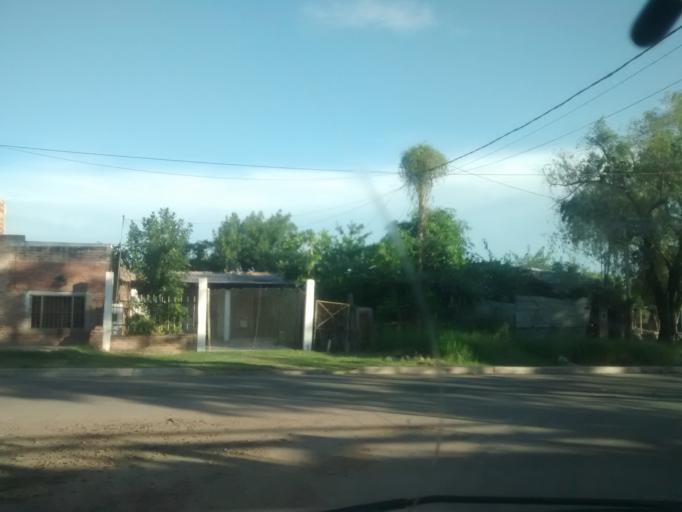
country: AR
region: Chaco
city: Resistencia
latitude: -27.4333
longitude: -58.9973
